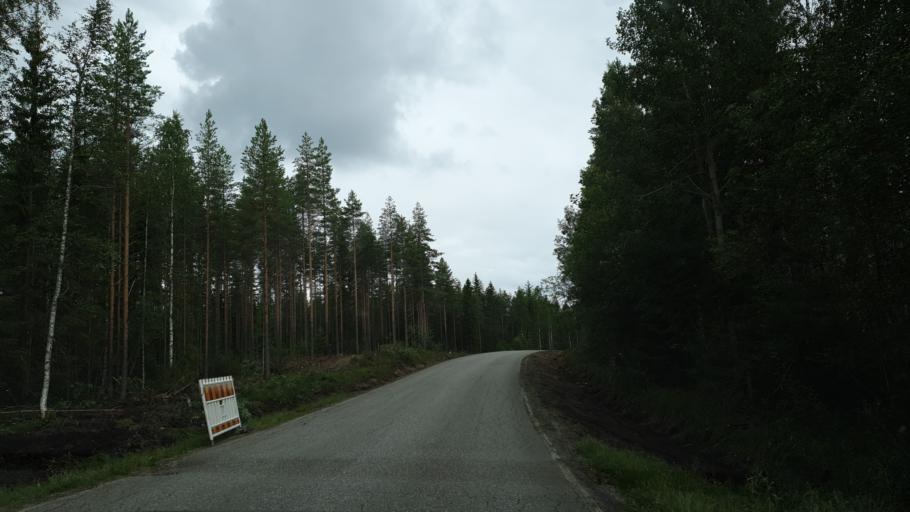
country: FI
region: Kainuu
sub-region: Kehys-Kainuu
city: Kuhmo
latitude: 64.1349
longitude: 29.4071
